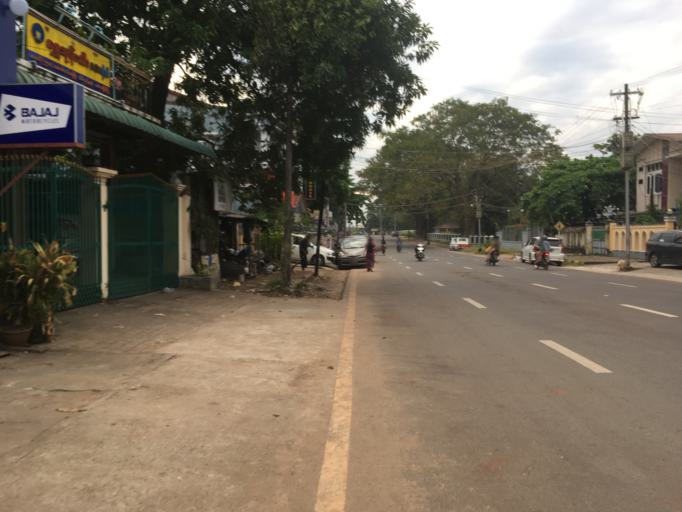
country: MM
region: Mon
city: Mawlamyine
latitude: 16.4697
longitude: 97.6226
